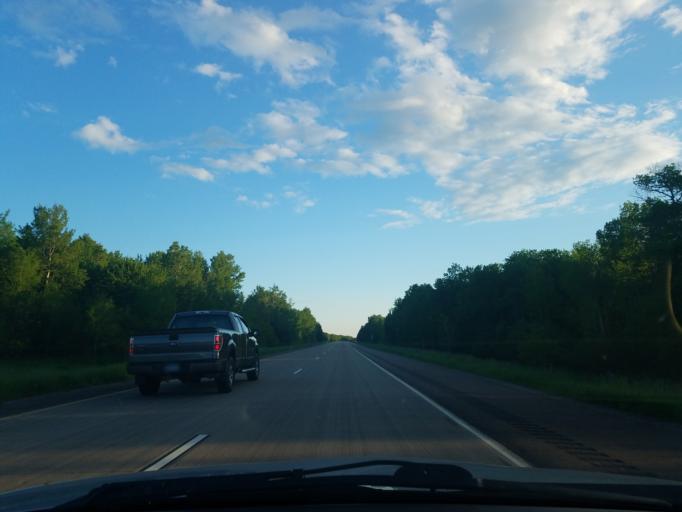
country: US
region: Minnesota
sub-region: Carlton County
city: Moose Lake
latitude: 46.5403
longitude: -92.6226
